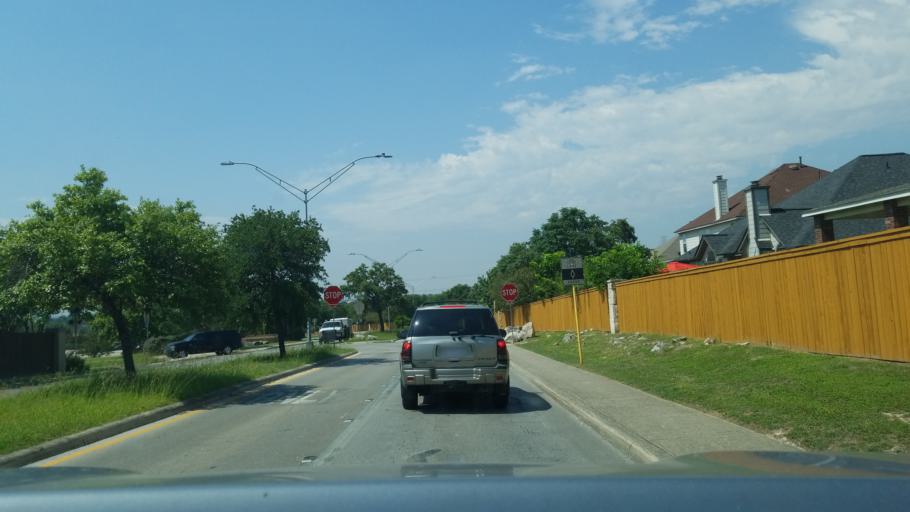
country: US
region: Texas
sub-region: Bexar County
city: Hollywood Park
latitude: 29.6365
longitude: -98.4442
